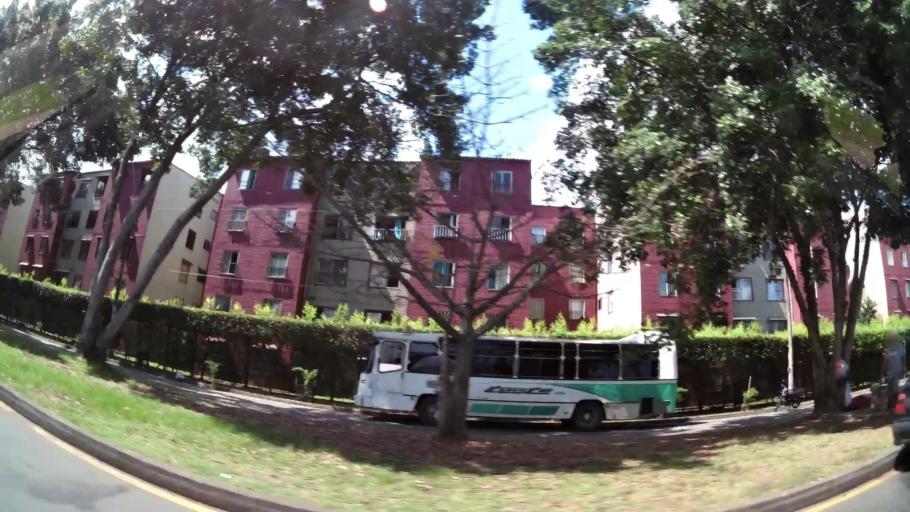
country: CO
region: Valle del Cauca
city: Cali
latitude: 3.3990
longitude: -76.5215
